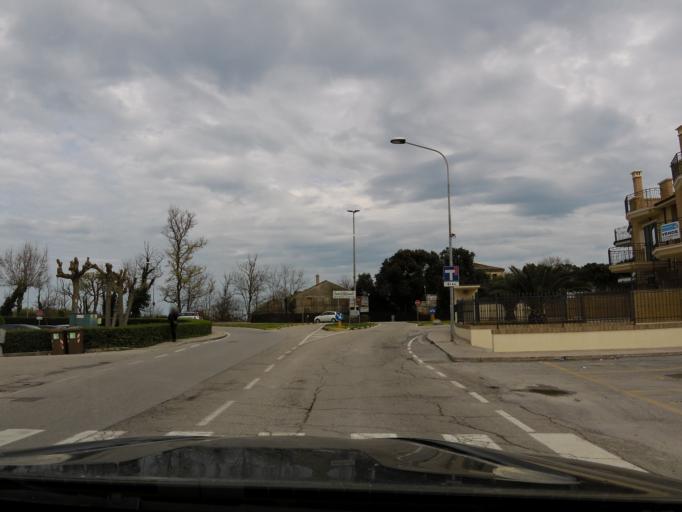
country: IT
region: The Marches
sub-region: Provincia di Macerata
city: Porto Recanati
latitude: 43.4210
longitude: 13.6688
